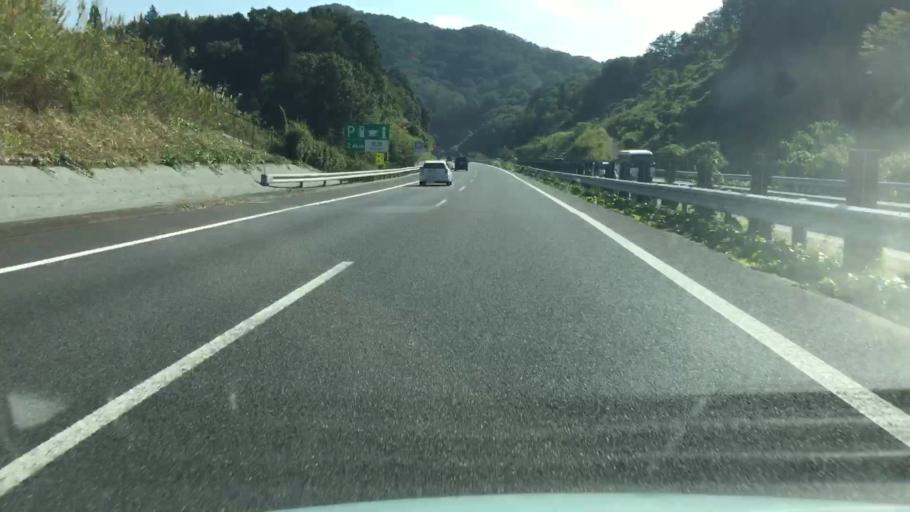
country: JP
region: Ibaraki
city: Kasama
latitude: 36.3403
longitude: 140.2259
